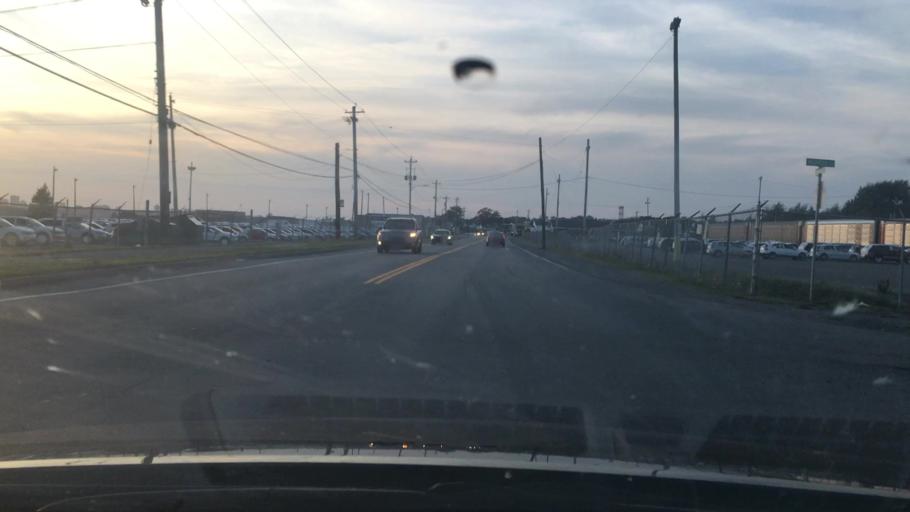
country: CA
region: Nova Scotia
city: Cole Harbour
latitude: 44.6211
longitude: -63.5072
